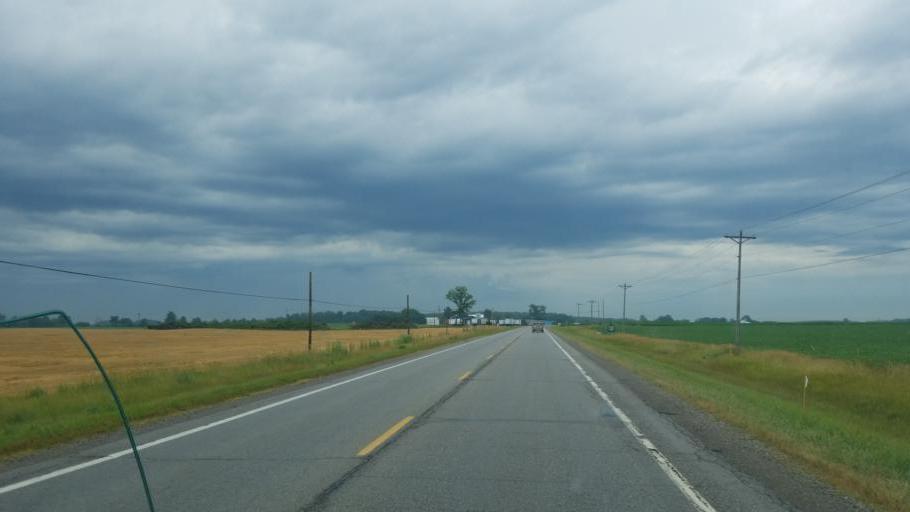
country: US
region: Ohio
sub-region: Williams County
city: Edgerton
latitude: 41.4481
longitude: -84.6952
